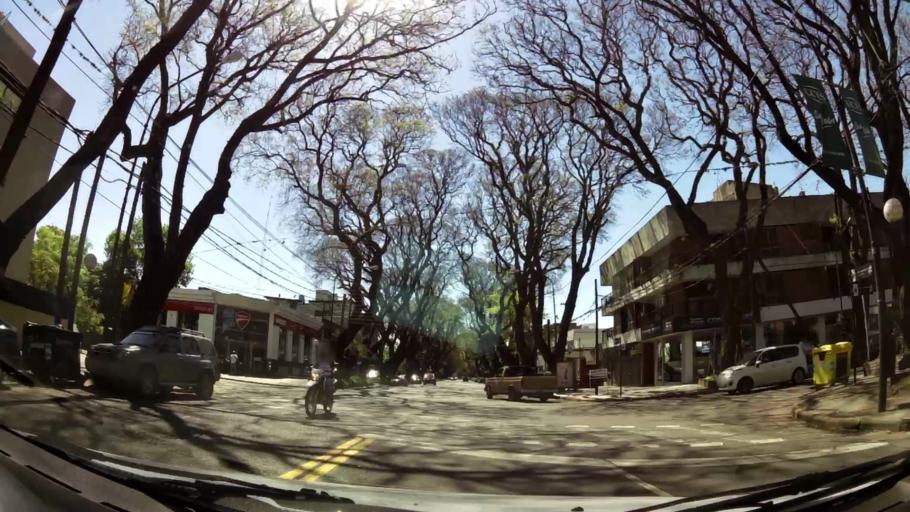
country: AR
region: Buenos Aires
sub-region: Partido de San Isidro
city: San Isidro
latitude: -34.4737
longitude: -58.5030
